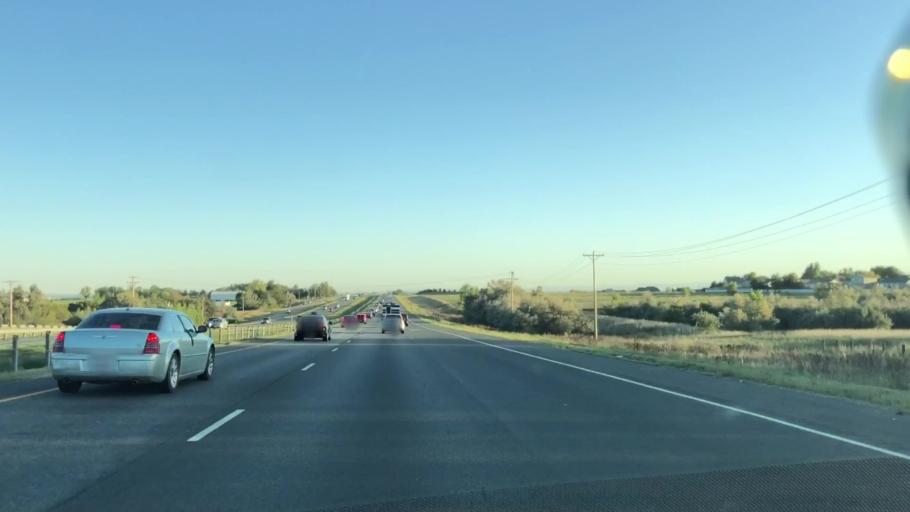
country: US
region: Colorado
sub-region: Weld County
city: Mead
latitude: 40.2609
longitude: -104.9787
